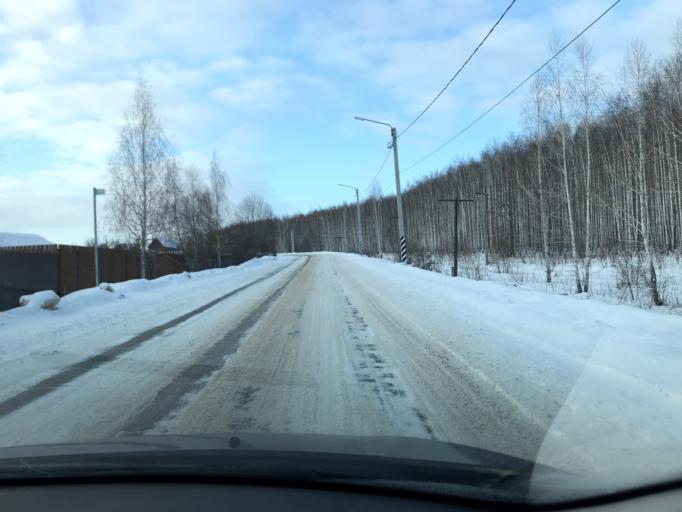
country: RU
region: Ulyanovsk
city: Undory
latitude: 54.6012
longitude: 48.4233
